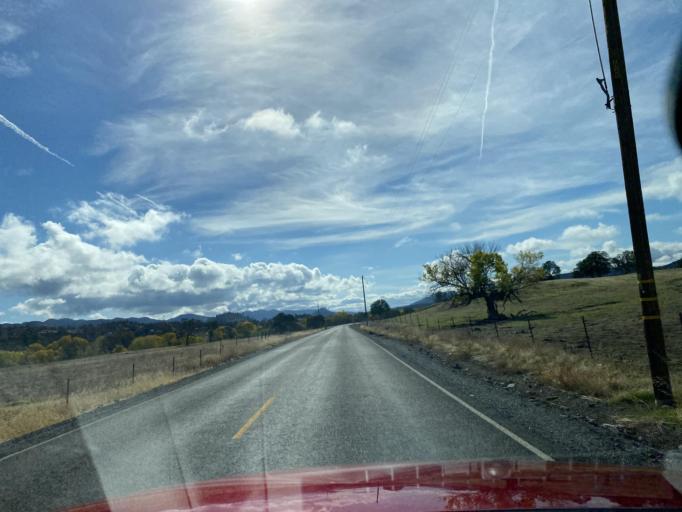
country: US
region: California
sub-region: Glenn County
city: Willows
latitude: 39.4664
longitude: -122.5118
